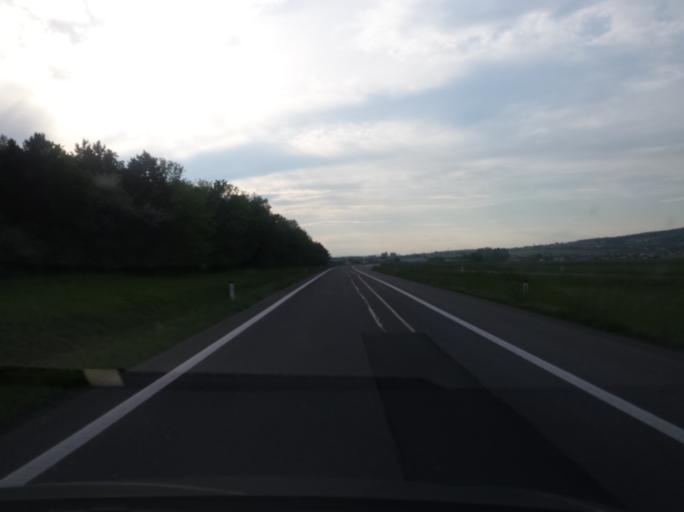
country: AT
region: Burgenland
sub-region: Eisenstadt-Umgebung
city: Wulkaprodersdorf
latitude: 47.8175
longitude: 16.4964
